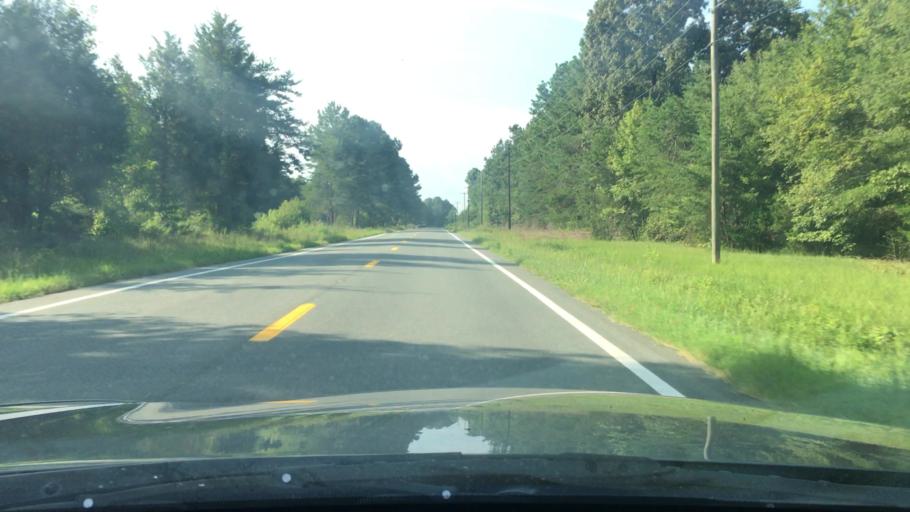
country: US
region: North Carolina
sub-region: Alamance County
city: Green Level
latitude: 36.2186
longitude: -79.3220
